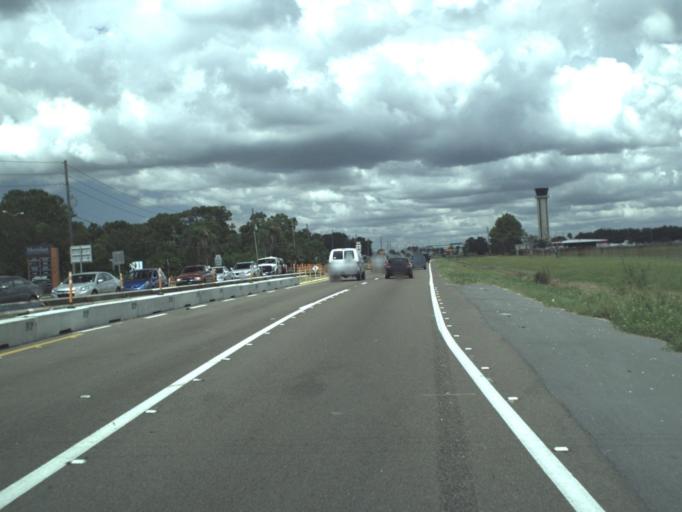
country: US
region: Florida
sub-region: Pinellas County
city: South Highpoint
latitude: 27.8974
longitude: -82.6929
